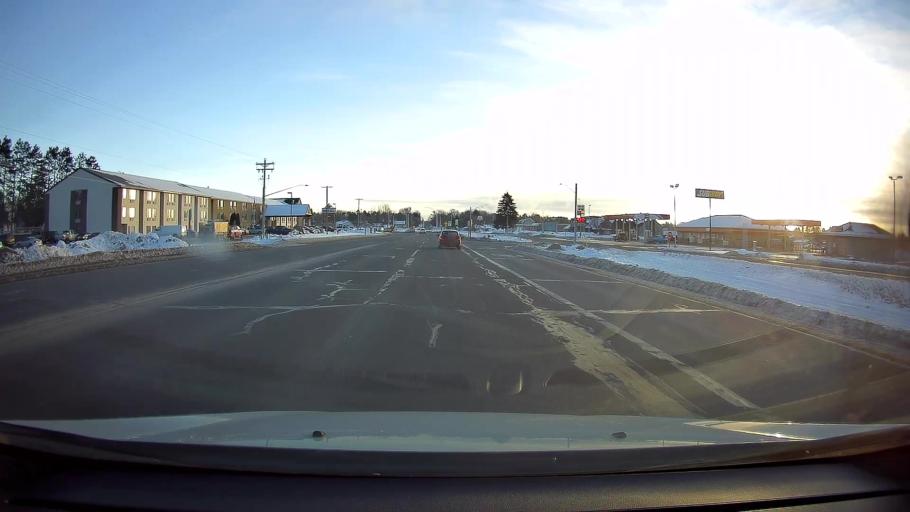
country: US
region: Wisconsin
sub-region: Barron County
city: Turtle Lake
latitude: 45.3953
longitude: -92.1562
